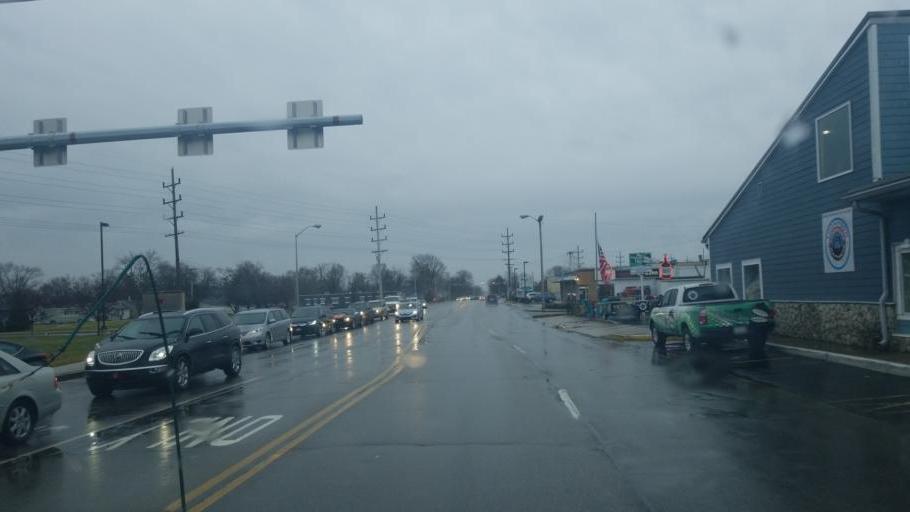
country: US
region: Indiana
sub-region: Bartholomew County
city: Columbus
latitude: 39.2228
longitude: -85.9043
